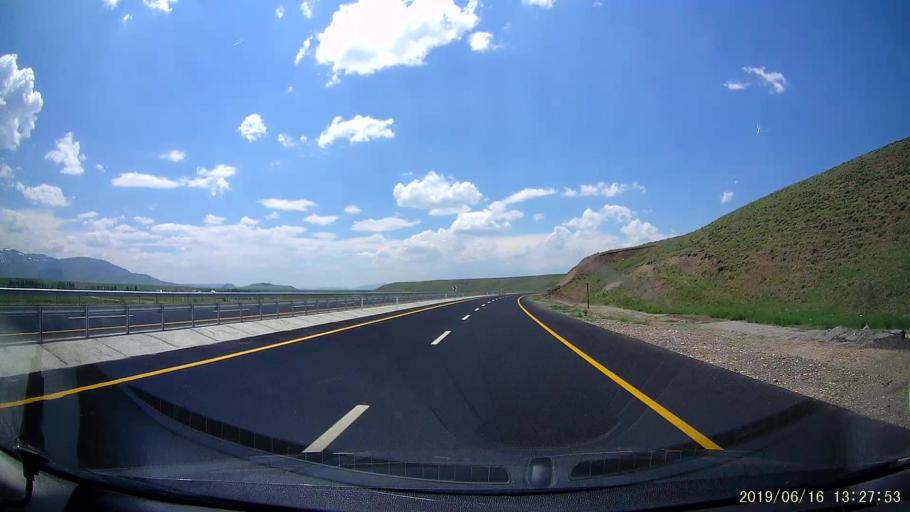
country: TR
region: Agri
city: Murat
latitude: 39.6712
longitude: 43.2992
